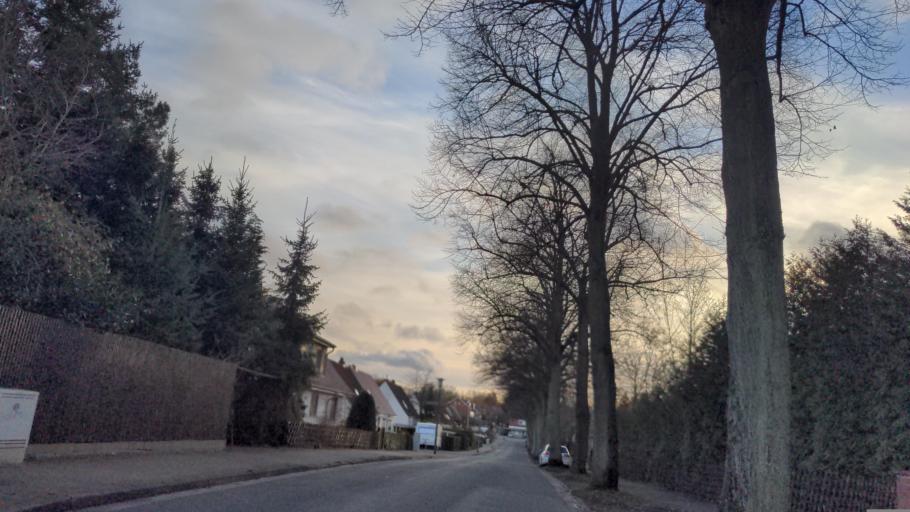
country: DE
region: Schleswig-Holstein
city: Neustadt in Holstein
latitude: 54.1071
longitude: 10.8261
